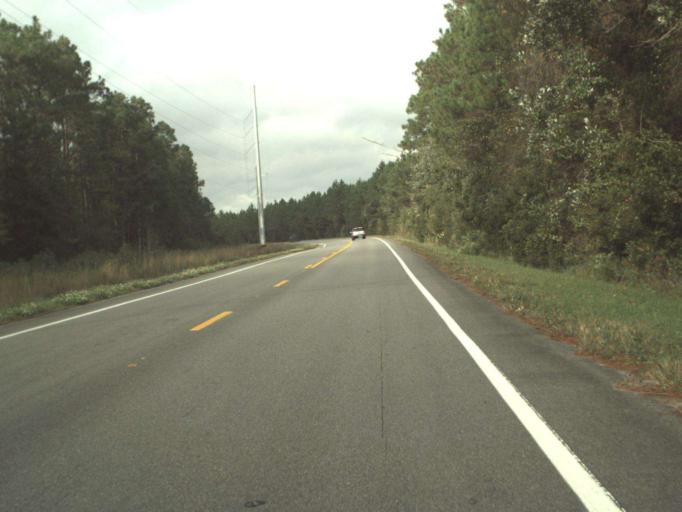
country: US
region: Florida
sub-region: Franklin County
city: Carrabelle
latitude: 29.9693
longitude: -84.4992
